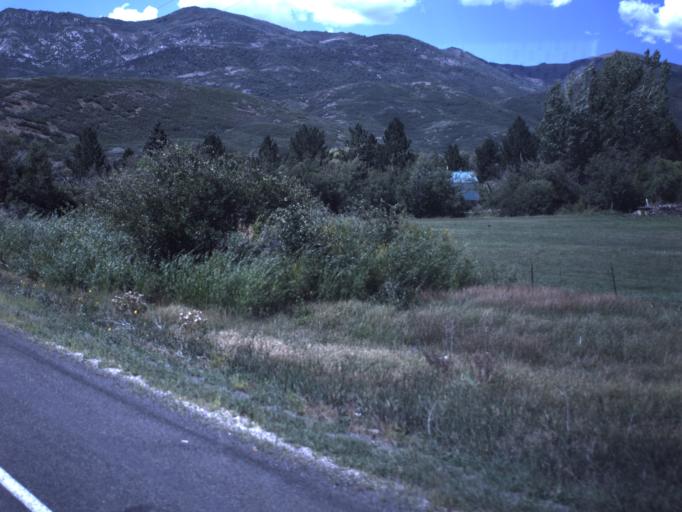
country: US
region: Utah
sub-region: Wasatch County
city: Heber
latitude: 40.5567
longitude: -111.4281
